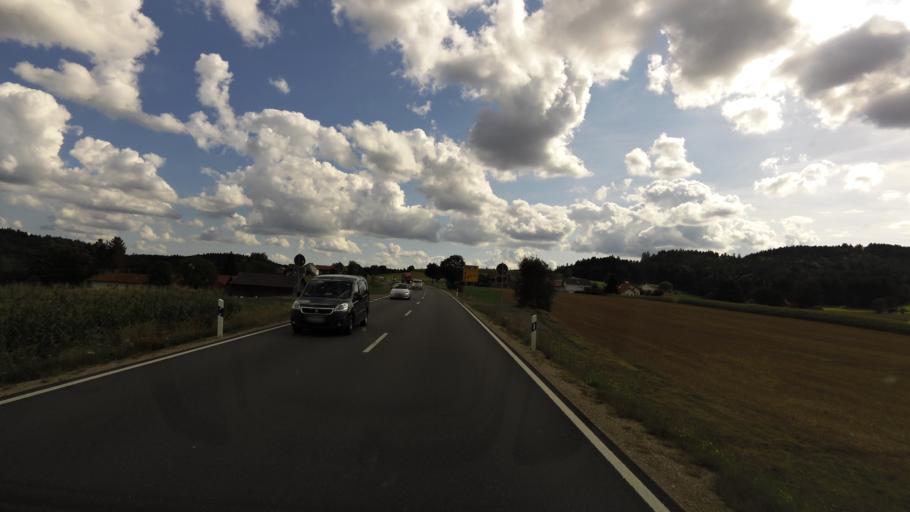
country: DE
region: Bavaria
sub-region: Upper Palatinate
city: Traitsching
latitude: 49.1209
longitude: 12.6503
